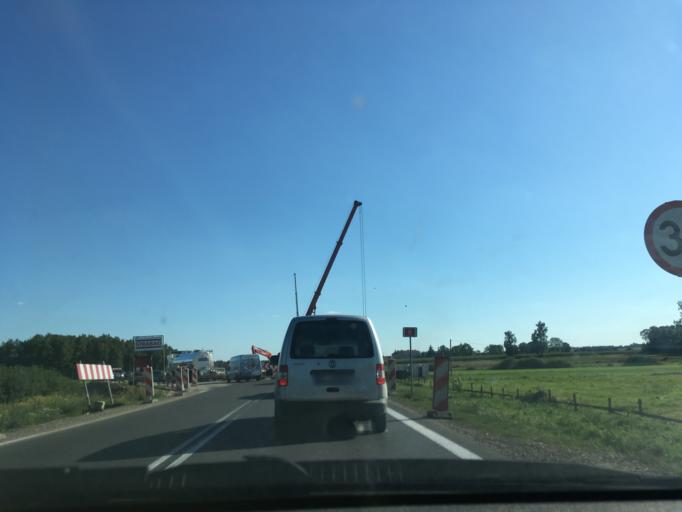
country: PL
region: Podlasie
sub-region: Powiat sokolski
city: Suchowola
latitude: 53.4554
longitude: 23.0878
